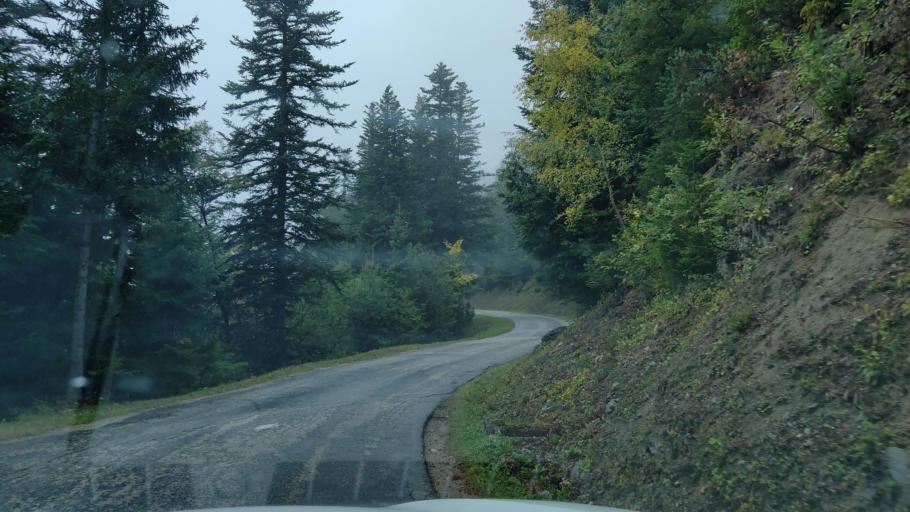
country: FR
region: Rhone-Alpes
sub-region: Departement de la Savoie
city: Modane
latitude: 45.2979
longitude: 6.8212
